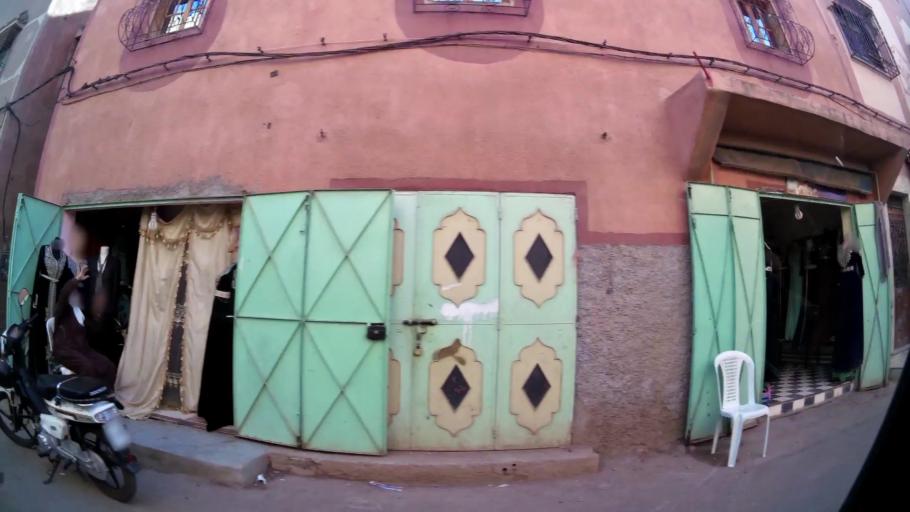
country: MA
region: Marrakech-Tensift-Al Haouz
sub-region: Marrakech
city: Marrakesh
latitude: 31.6093
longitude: -7.9626
